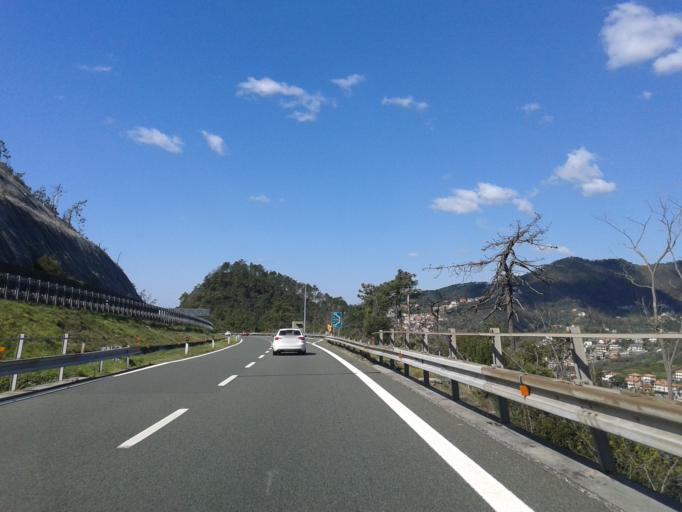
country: IT
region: Liguria
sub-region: Provincia di Genova
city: Casarza Ligure
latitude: 44.2711
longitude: 9.4698
